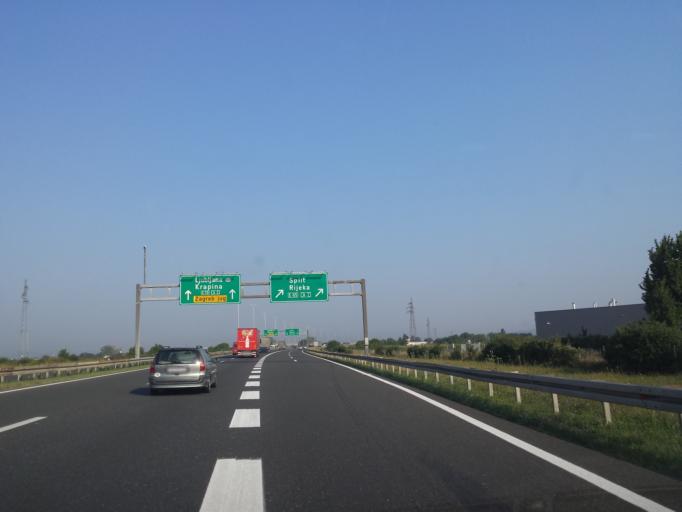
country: HR
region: Grad Zagreb
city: Zadvorsko
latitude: 45.7522
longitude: 15.9090
